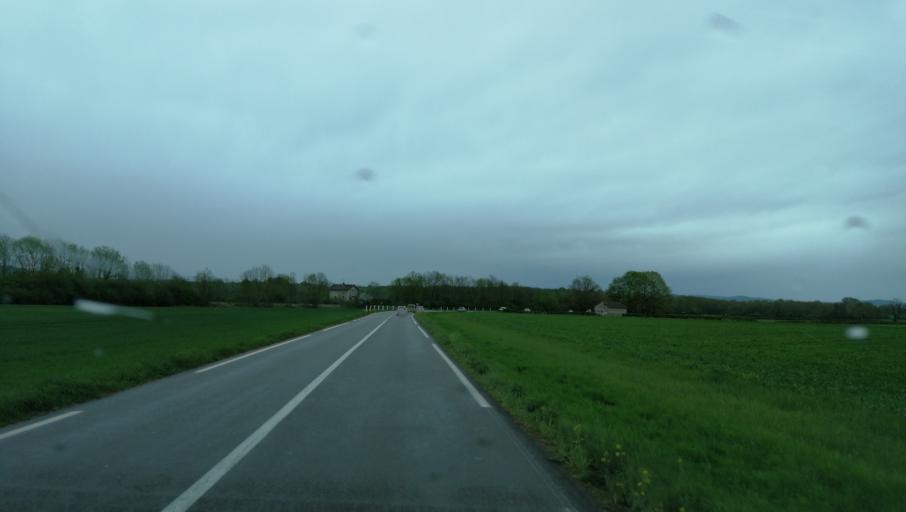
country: FR
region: Franche-Comte
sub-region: Departement du Jura
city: Bletterans
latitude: 46.7306
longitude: 5.4699
